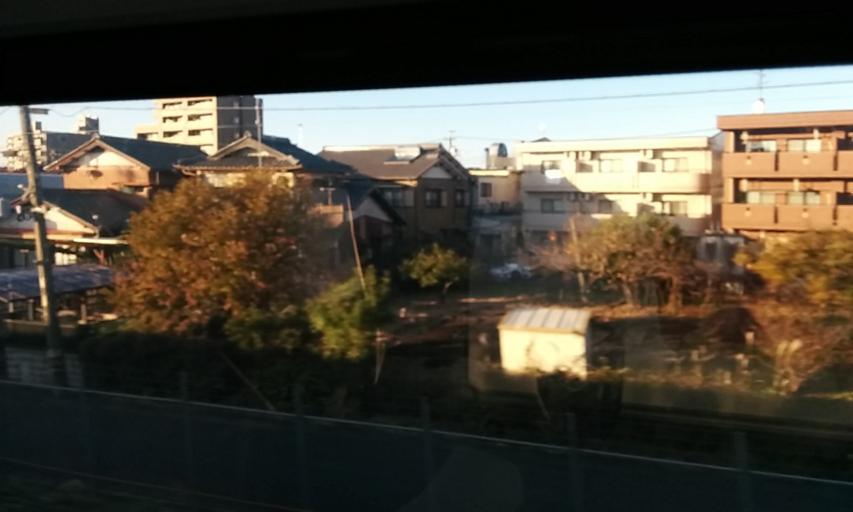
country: JP
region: Aichi
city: Kasugai
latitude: 35.2642
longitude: 137.0364
